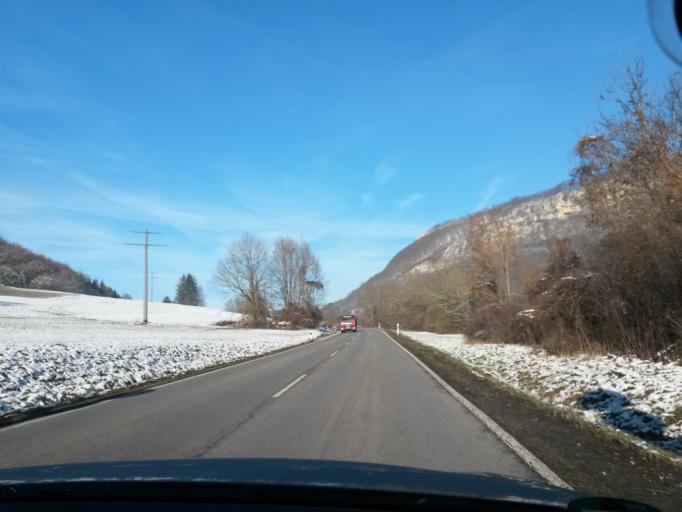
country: DE
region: Baden-Wuerttemberg
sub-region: Regierungsbezirk Stuttgart
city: Bad Uberkingen
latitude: 48.6010
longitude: 9.7794
